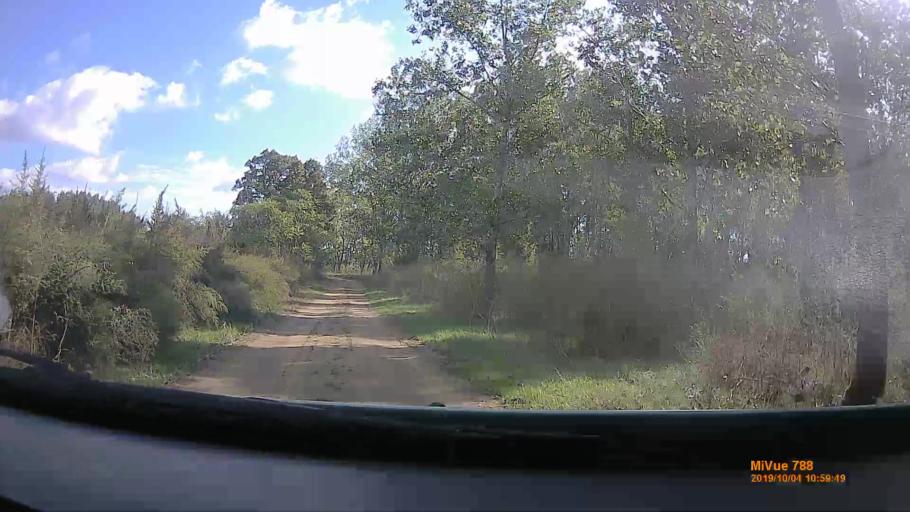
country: HU
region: Szabolcs-Szatmar-Bereg
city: Nyirtelek
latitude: 47.9812
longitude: 21.6683
